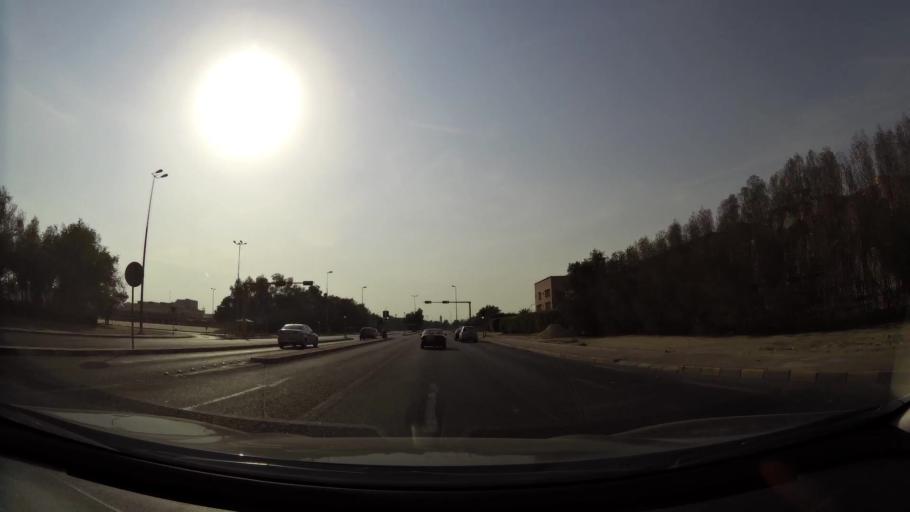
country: KW
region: Al Ahmadi
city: Ar Riqqah
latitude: 29.1663
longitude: 48.0890
